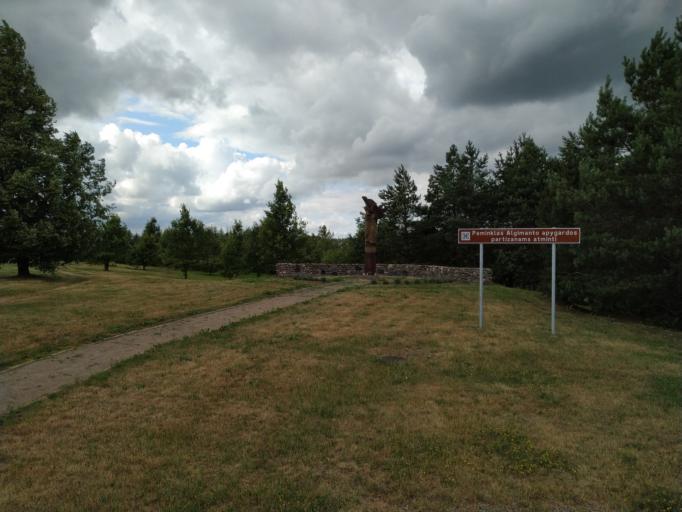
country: LT
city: Kupiskis
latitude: 55.8437
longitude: 24.9871
